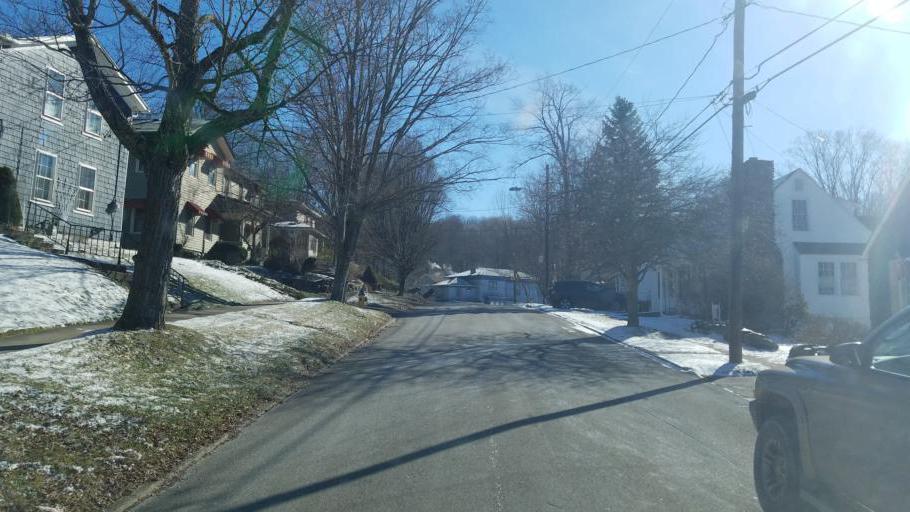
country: US
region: New York
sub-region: Allegany County
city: Wellsville
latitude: 42.1259
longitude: -77.9446
